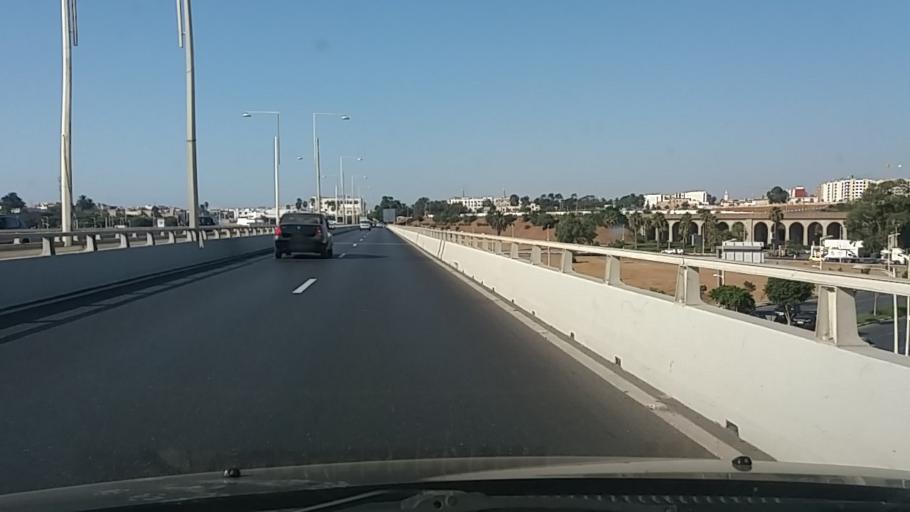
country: MA
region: Rabat-Sale-Zemmour-Zaer
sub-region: Rabat
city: Rabat
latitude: 34.0311
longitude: -6.8184
